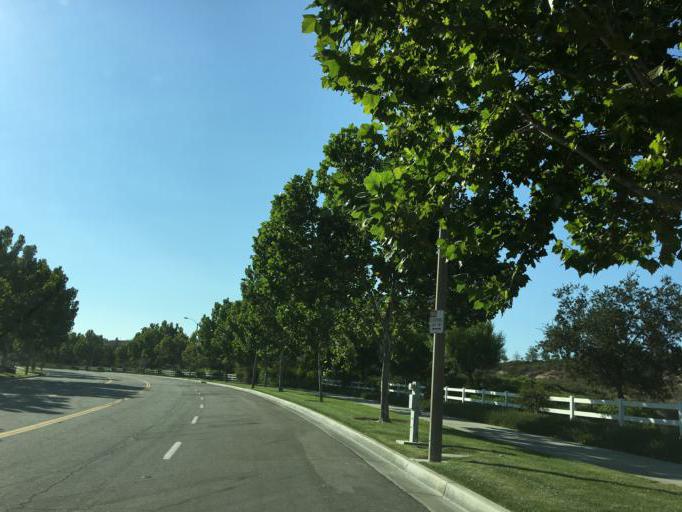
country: US
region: California
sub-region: Los Angeles County
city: Valencia
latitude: 34.4072
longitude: -118.5973
